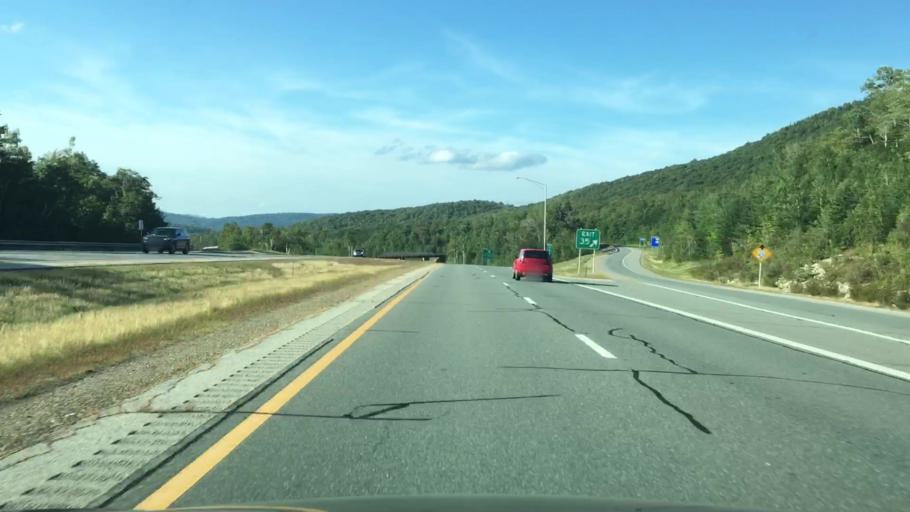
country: US
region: New Hampshire
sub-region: Grafton County
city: Deerfield
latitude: 44.1946
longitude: -71.6814
